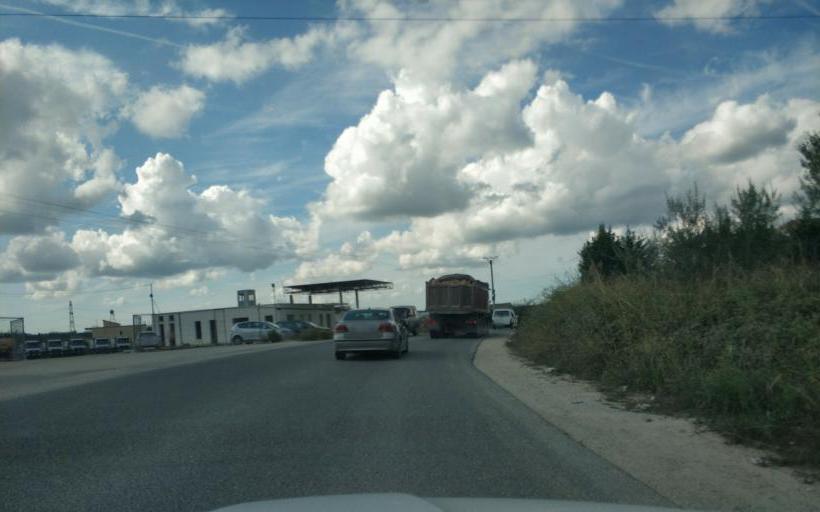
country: AL
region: Durres
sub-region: Rrethi i Krujes
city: Fushe-Kruje
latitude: 41.4760
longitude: 19.7488
